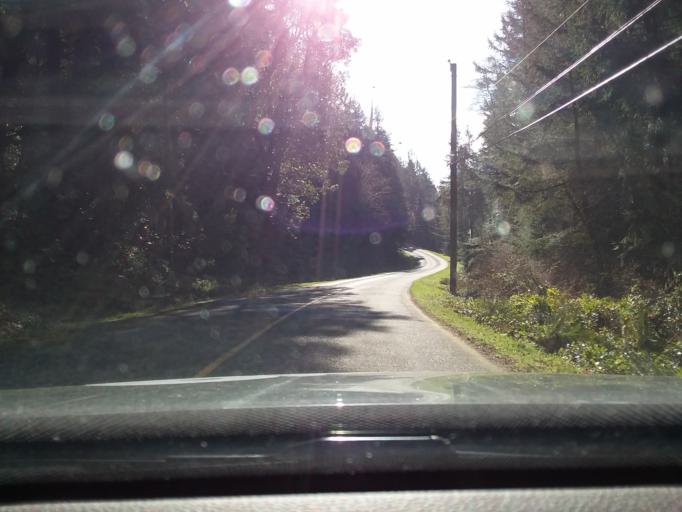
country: CA
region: British Columbia
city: North Cowichan
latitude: 48.9496
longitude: -123.5250
